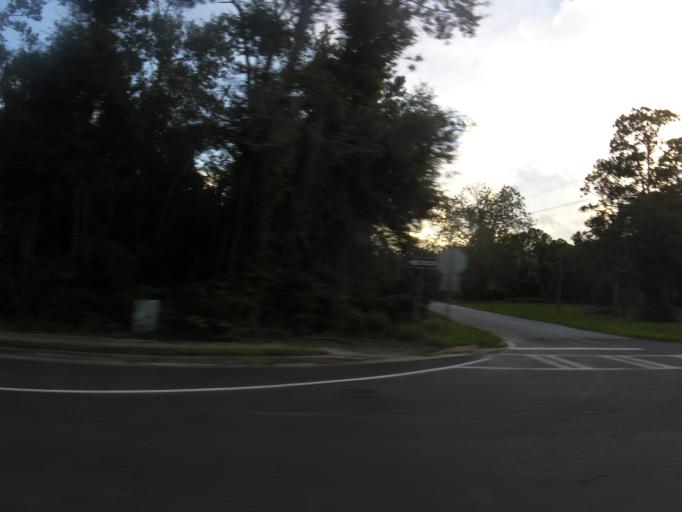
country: US
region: Georgia
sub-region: Camden County
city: St Marys
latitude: 30.7558
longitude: -81.5927
